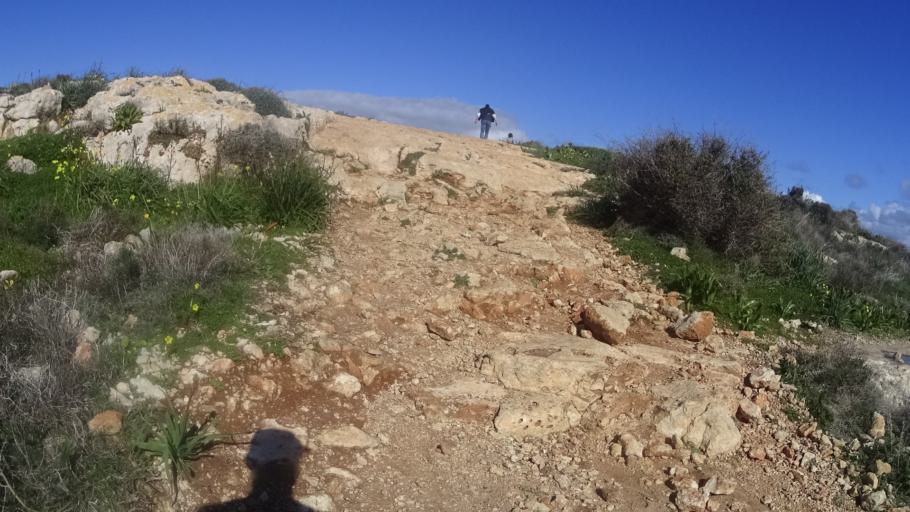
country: MT
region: Saint Paul's Bay
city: San Pawl il-Bahar
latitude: 35.9602
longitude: 14.3945
